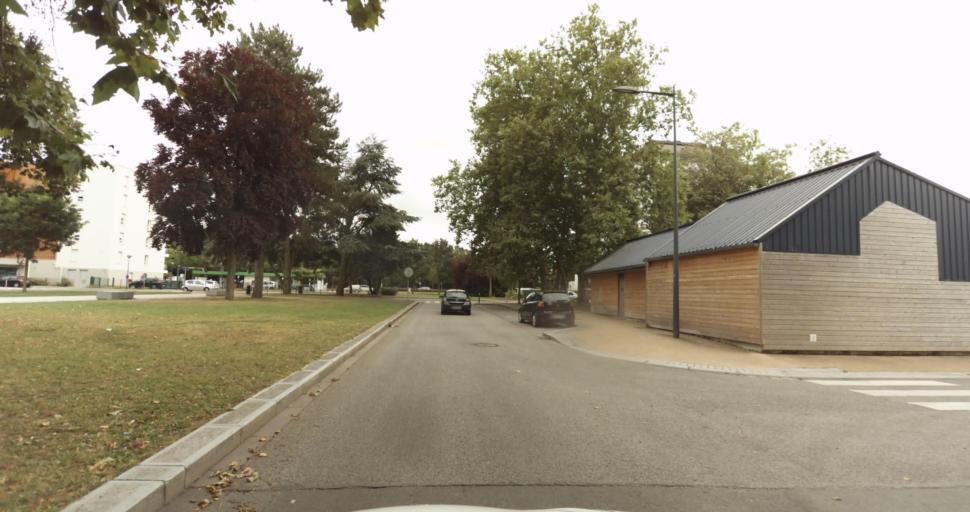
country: FR
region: Haute-Normandie
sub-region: Departement de l'Eure
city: Evreux
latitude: 49.0059
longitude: 1.1574
